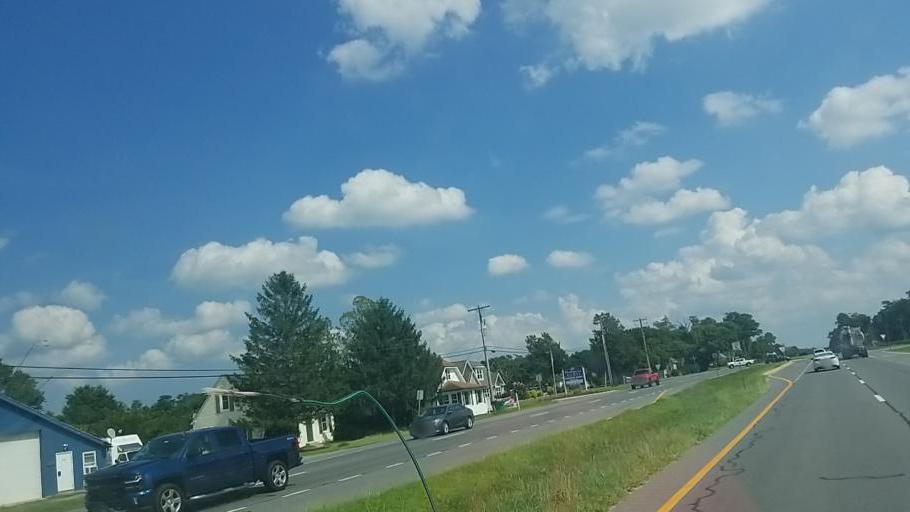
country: US
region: Delaware
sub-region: Sussex County
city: Georgetown
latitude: 38.6349
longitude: -75.3511
